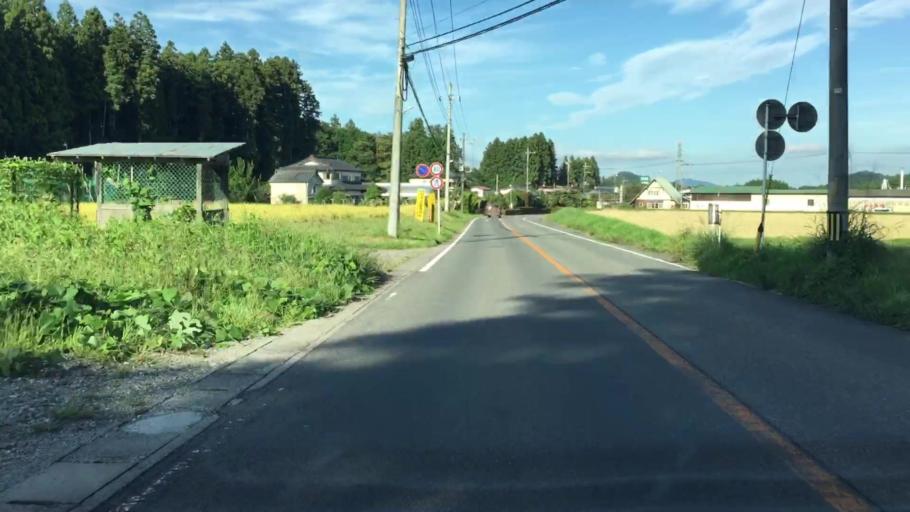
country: JP
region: Tochigi
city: Imaichi
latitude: 36.7362
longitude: 139.7025
